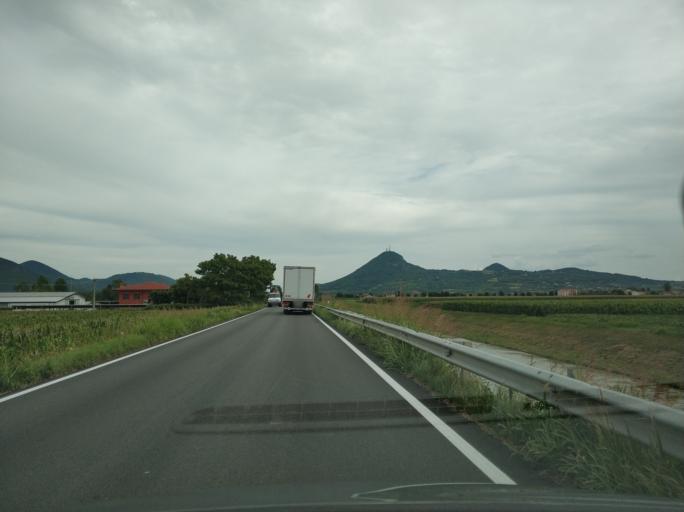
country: IT
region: Veneto
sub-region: Provincia di Padova
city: Lozzo Atestino
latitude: 45.2636
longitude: 11.6107
